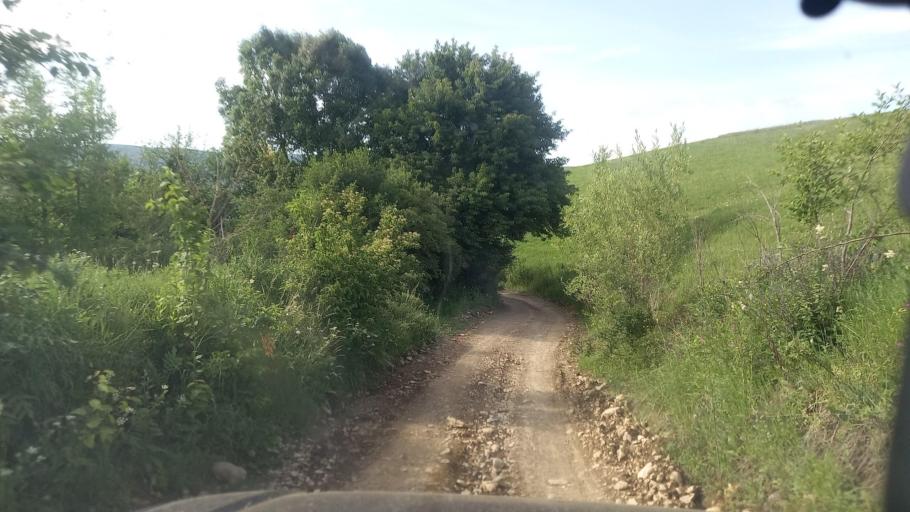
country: RU
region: Krasnodarskiy
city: Peredovaya
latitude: 44.0745
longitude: 41.3645
